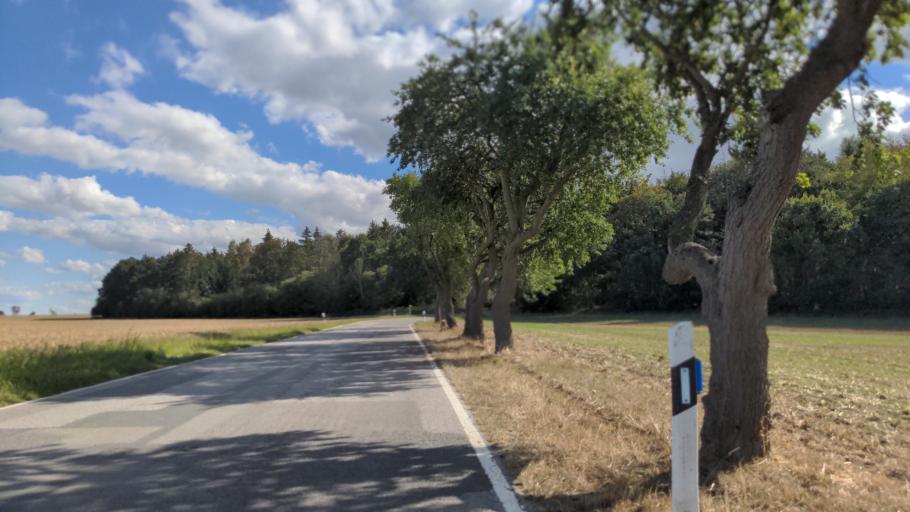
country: DE
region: Mecklenburg-Vorpommern
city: Gramkow
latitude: 53.9169
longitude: 11.3755
